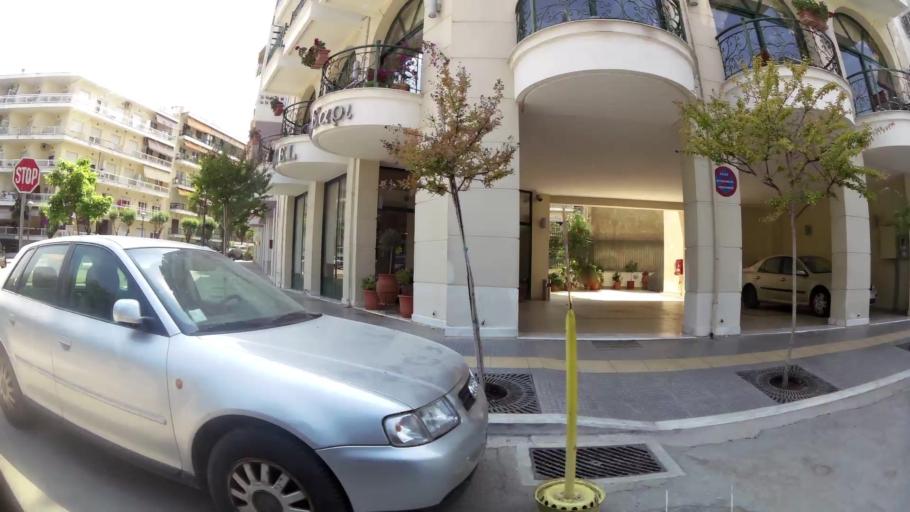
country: GR
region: Central Macedonia
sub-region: Nomos Imathias
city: Veroia
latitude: 40.5253
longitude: 22.2072
